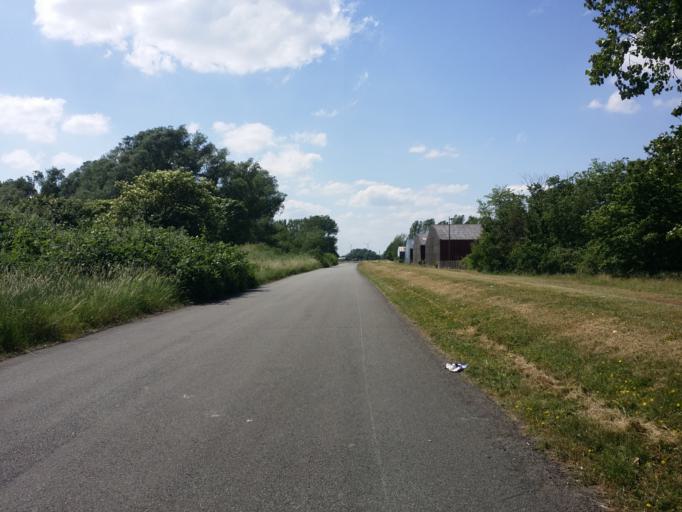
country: DE
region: Lower Saxony
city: Lemwerder
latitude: 53.1214
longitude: 8.6646
